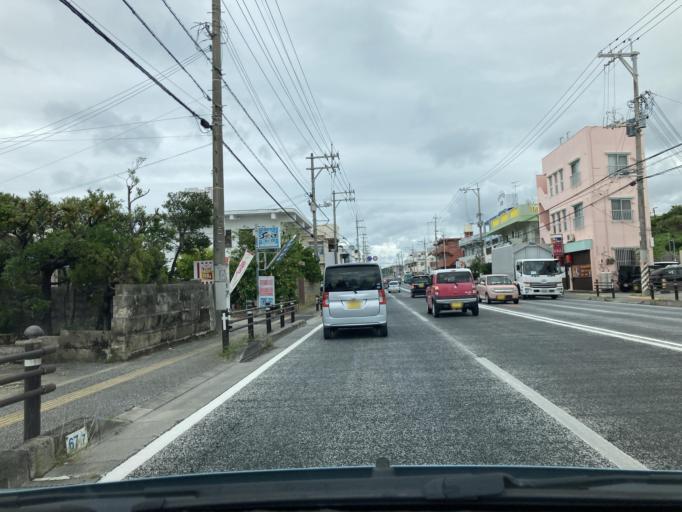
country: JP
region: Okinawa
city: Tomigusuku
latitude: 26.2008
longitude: 127.7439
